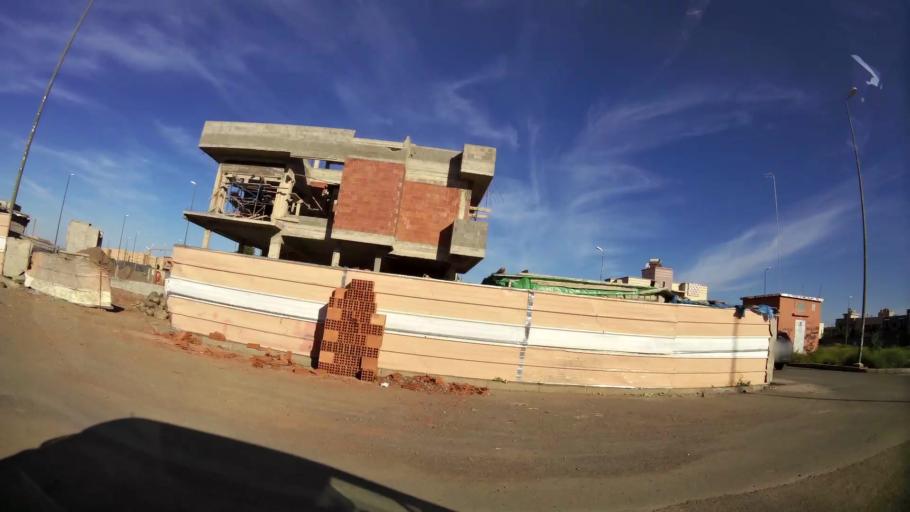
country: MA
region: Marrakech-Tensift-Al Haouz
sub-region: Marrakech
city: Marrakesh
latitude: 31.6718
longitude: -8.0708
